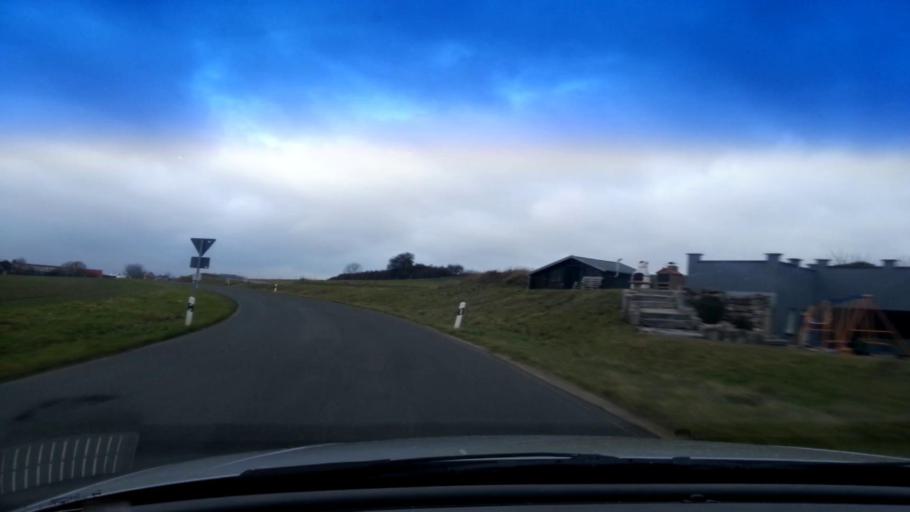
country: DE
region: Bavaria
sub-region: Upper Franconia
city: Walsdorf
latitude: 49.8284
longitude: 10.7849
